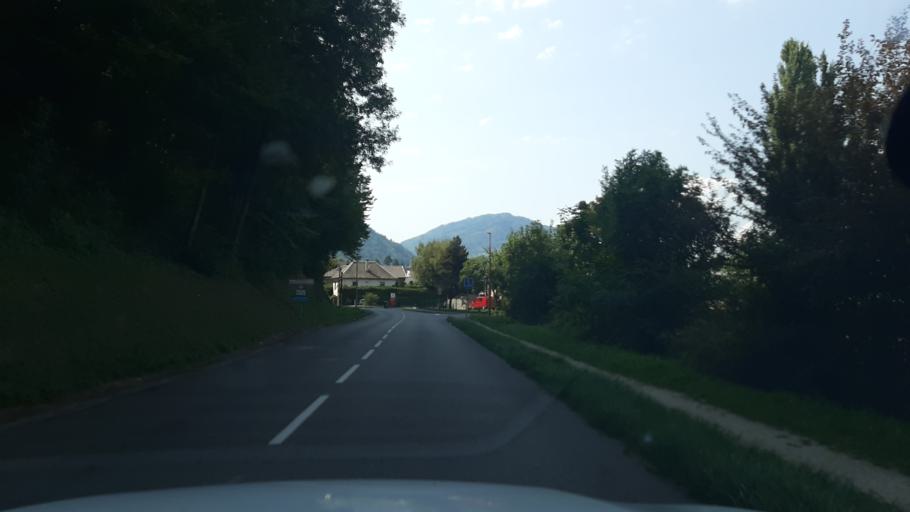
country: FR
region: Rhone-Alpes
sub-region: Departement de la Savoie
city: La Rochette
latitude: 45.4619
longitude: 6.1229
